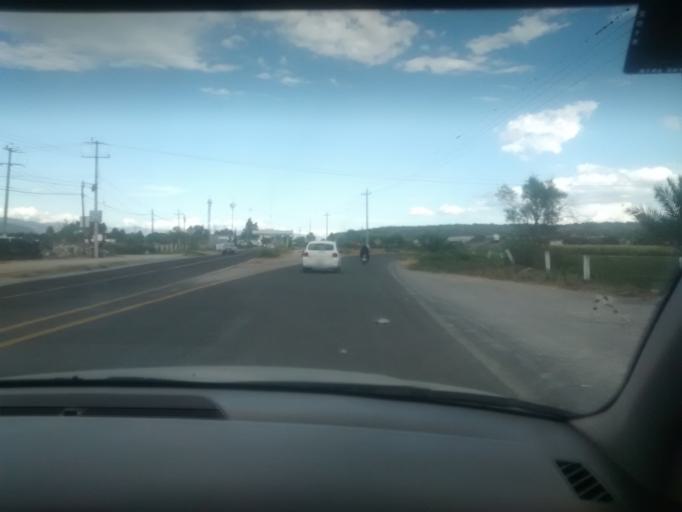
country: MX
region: Puebla
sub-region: Santiago Miahuatlan
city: San Jose Monte Chiquito
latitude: 18.4889
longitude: -97.4591
